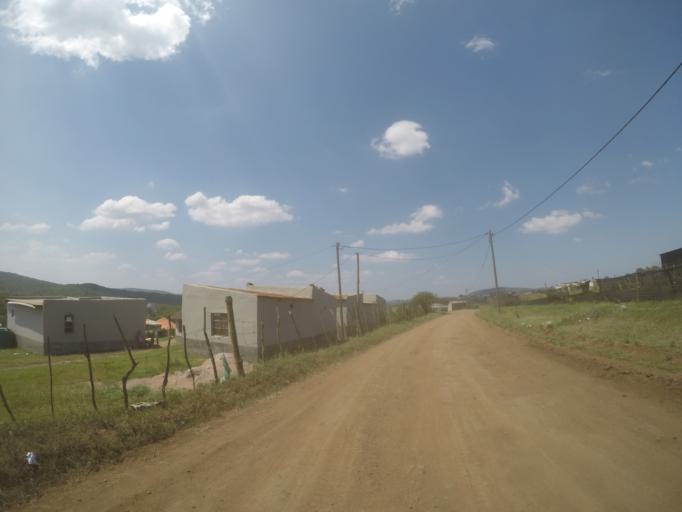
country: ZA
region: KwaZulu-Natal
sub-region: uThungulu District Municipality
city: Empangeni
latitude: -28.5883
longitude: 31.7430
